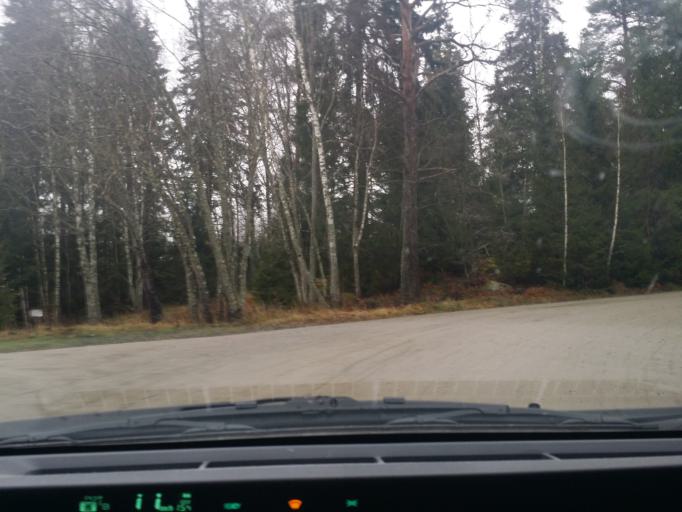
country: SE
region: Vaestmanland
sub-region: Vasteras
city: Skultuna
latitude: 59.7760
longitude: 16.3316
